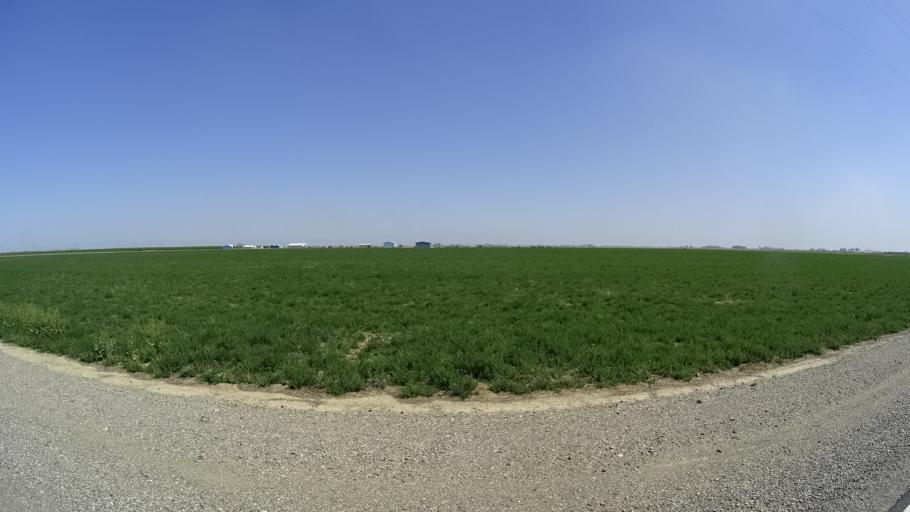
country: US
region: California
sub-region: Glenn County
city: Willows
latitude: 39.6004
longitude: -122.1375
